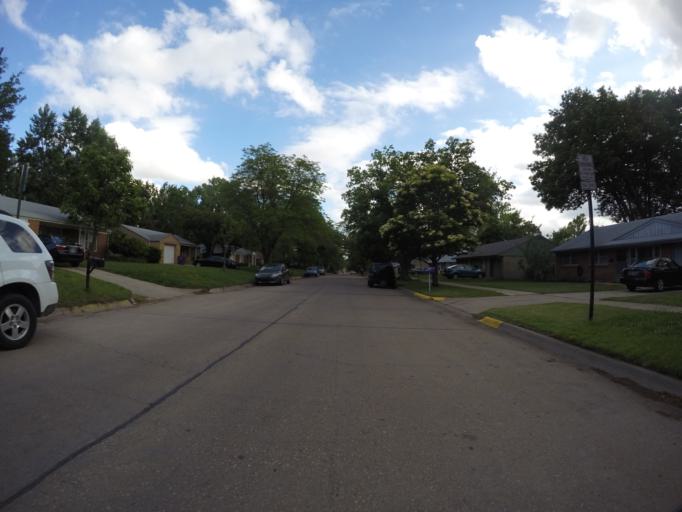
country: US
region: Kansas
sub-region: Riley County
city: Manhattan
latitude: 39.1952
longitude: -96.5920
